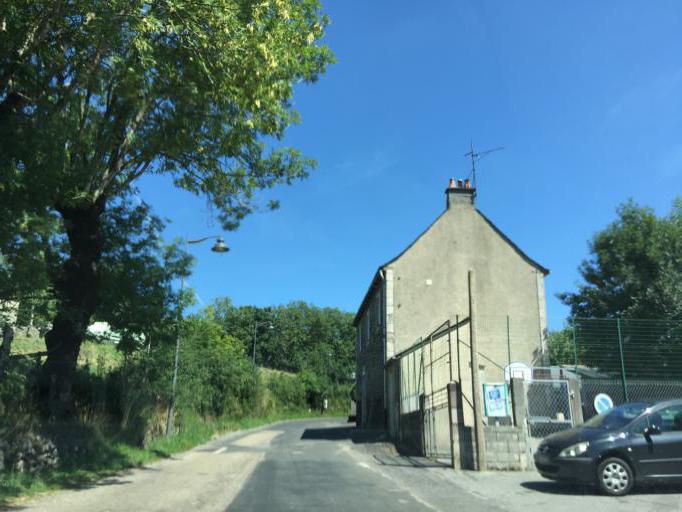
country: FR
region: Midi-Pyrenees
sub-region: Departement de l'Aveyron
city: Laguiole
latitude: 44.6526
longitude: 2.8669
